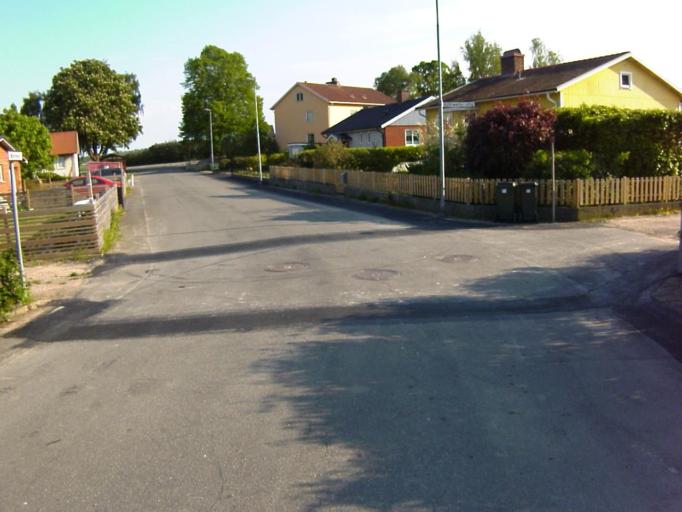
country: SE
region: Skane
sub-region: Kristianstads Kommun
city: Onnestad
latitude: 56.0583
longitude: 14.0301
